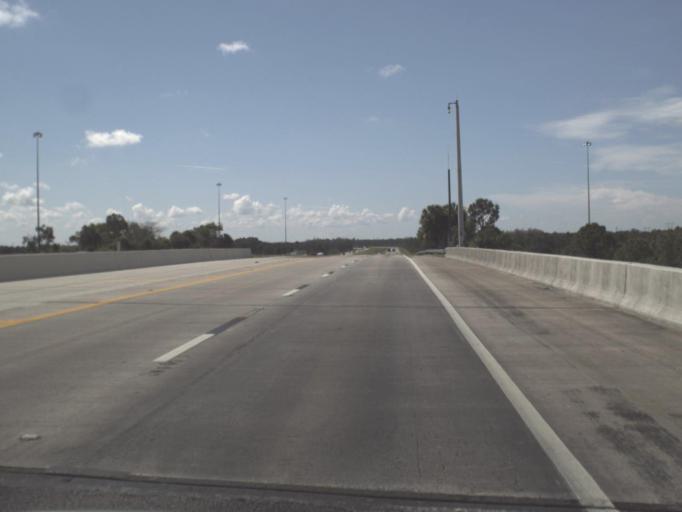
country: US
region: Florida
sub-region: Charlotte County
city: Charlotte Park
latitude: 26.8585
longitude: -81.9714
